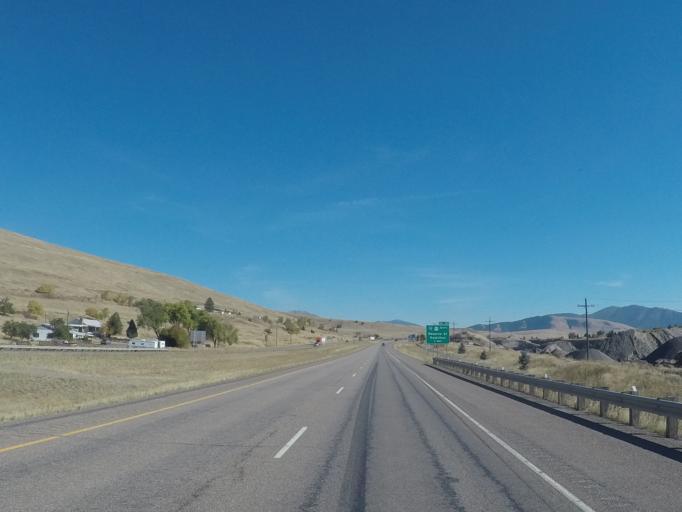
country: US
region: Montana
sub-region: Missoula County
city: Orchard Homes
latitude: 46.9188
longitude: -114.0539
